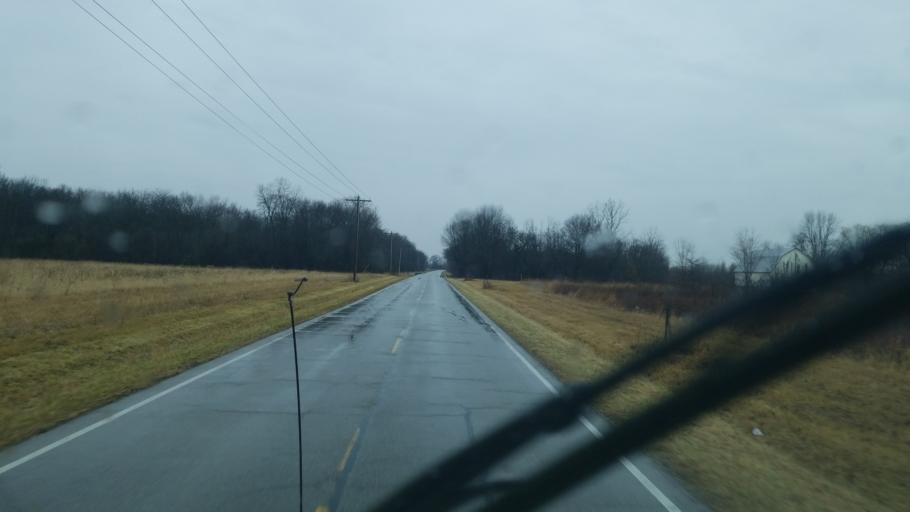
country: US
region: Ohio
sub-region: Union County
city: Richwood
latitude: 40.5716
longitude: -83.2941
